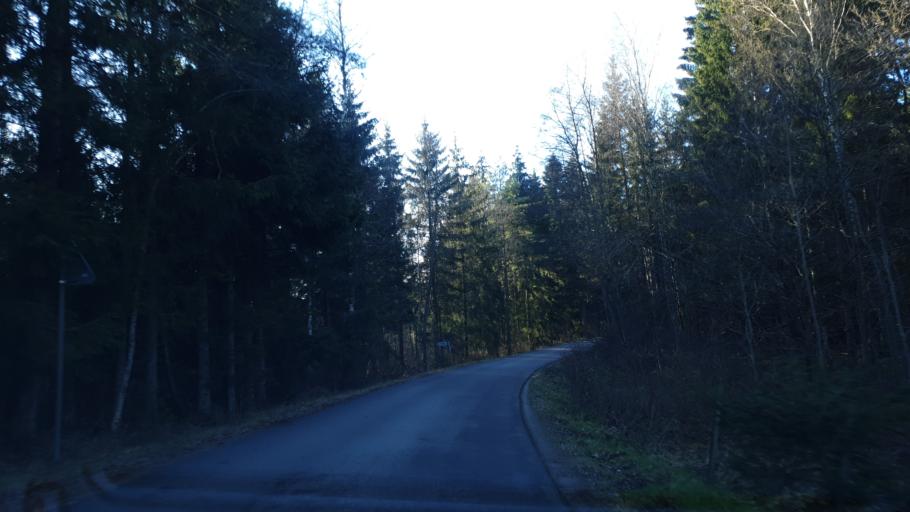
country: SE
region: Blekinge
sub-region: Karlskrona Kommun
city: Nattraby
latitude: 56.2656
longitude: 15.4478
